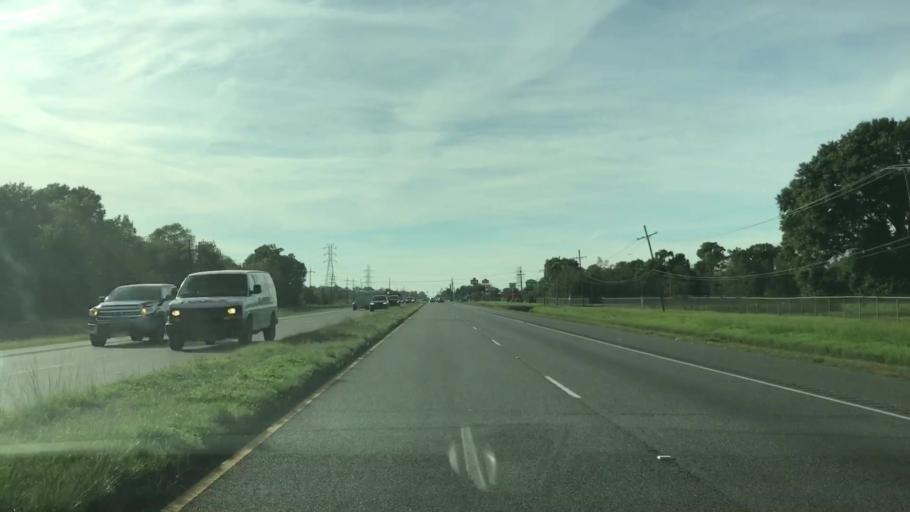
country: US
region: Louisiana
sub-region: Jefferson Parish
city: Avondale
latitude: 29.9097
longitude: -90.1975
